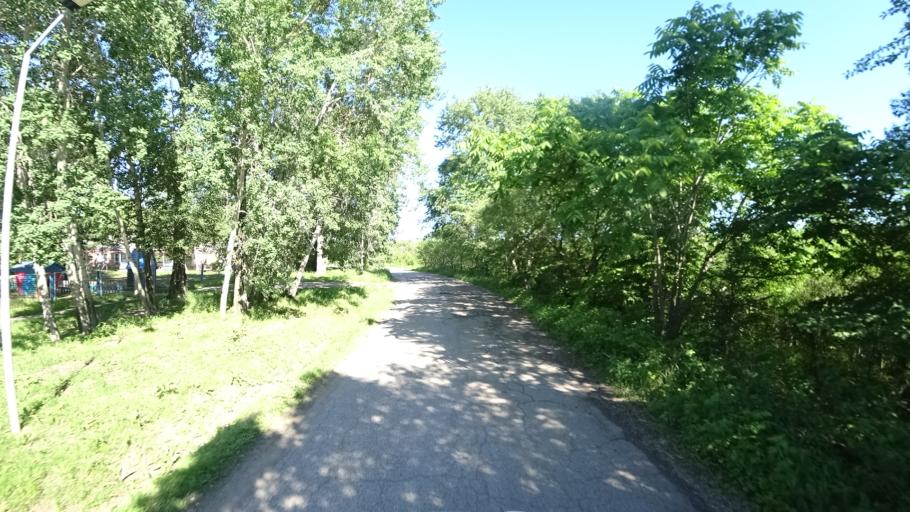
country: RU
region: Khabarovsk Krai
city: Khor
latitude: 47.8856
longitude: 134.9970
